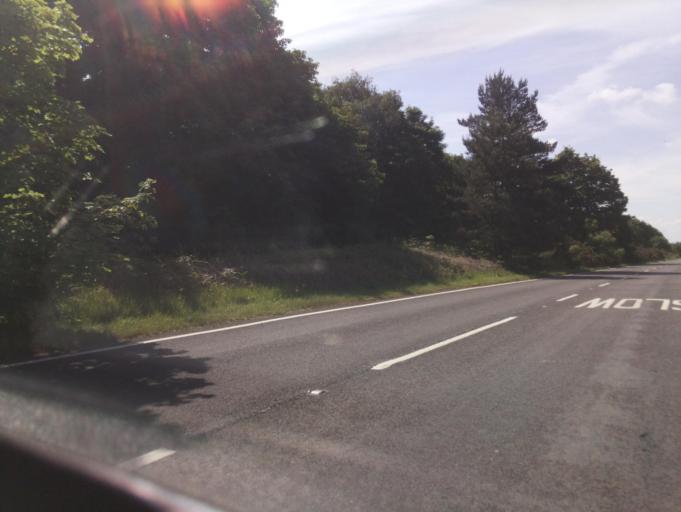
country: GB
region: England
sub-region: North Lincolnshire
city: Manton
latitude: 53.5270
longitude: -0.5784
